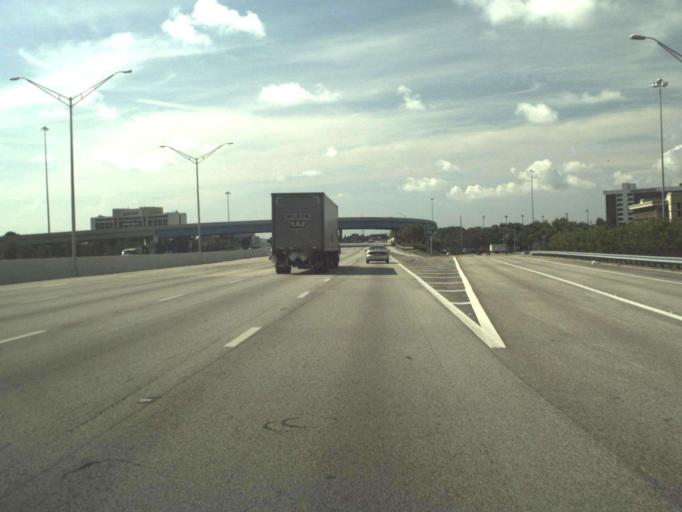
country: US
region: Florida
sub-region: Palm Beach County
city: North Palm Beach
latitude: 26.8428
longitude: -80.1043
